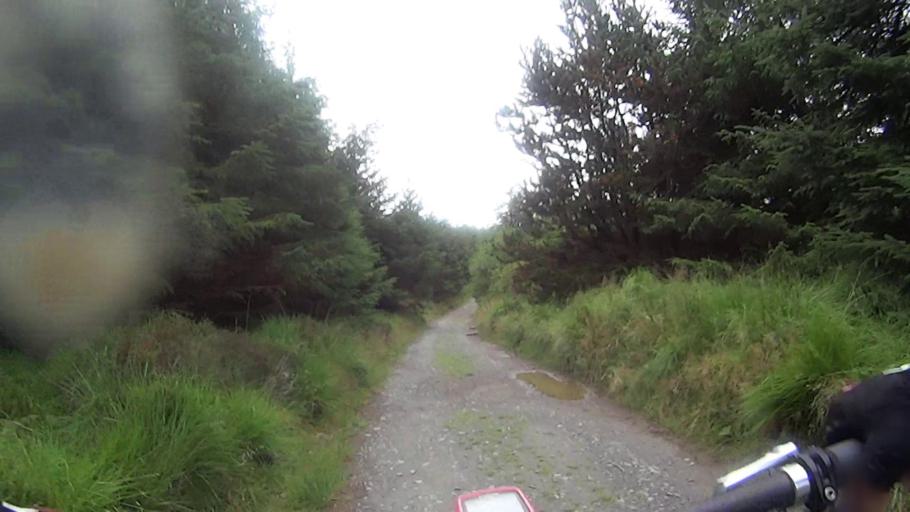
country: GB
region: Wales
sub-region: County of Ceredigion
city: Bow Street
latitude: 52.4234
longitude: -3.8800
